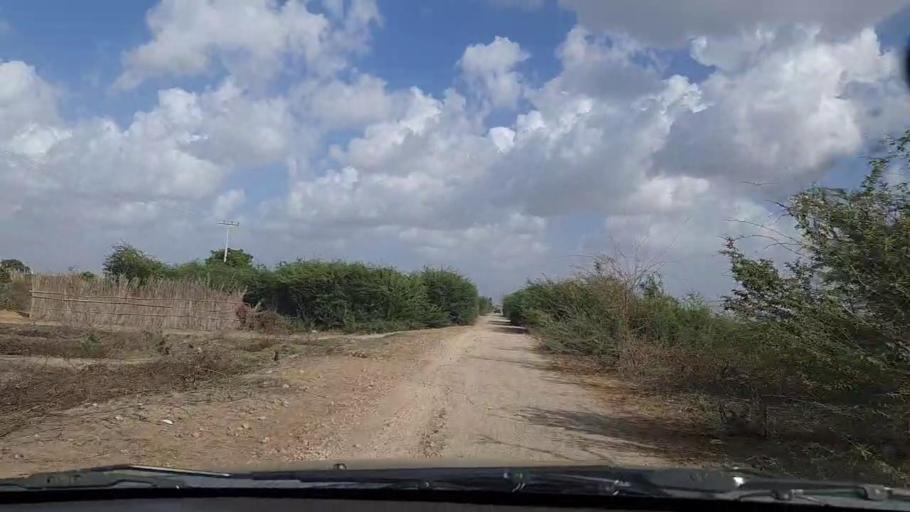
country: PK
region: Sindh
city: Keti Bandar
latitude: 24.0975
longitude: 67.6049
